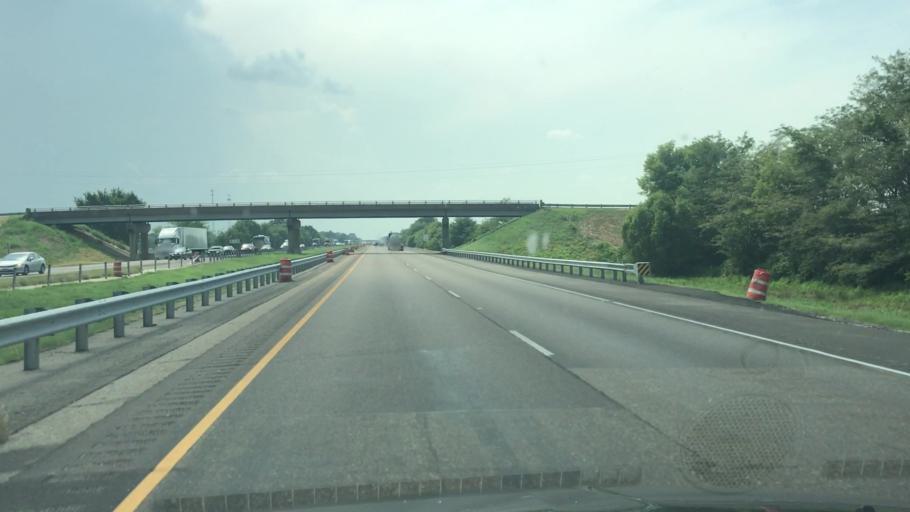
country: US
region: Arkansas
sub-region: Crittenden County
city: Earle
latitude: 35.1335
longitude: -90.4658
